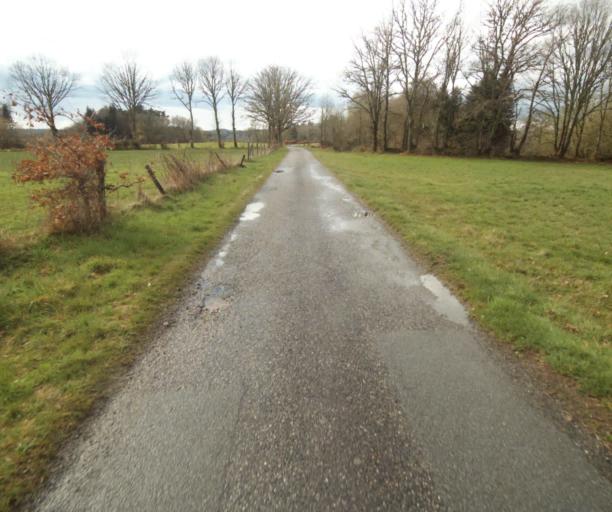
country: FR
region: Limousin
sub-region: Departement de la Correze
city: Saint-Privat
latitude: 45.2424
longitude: 2.0055
